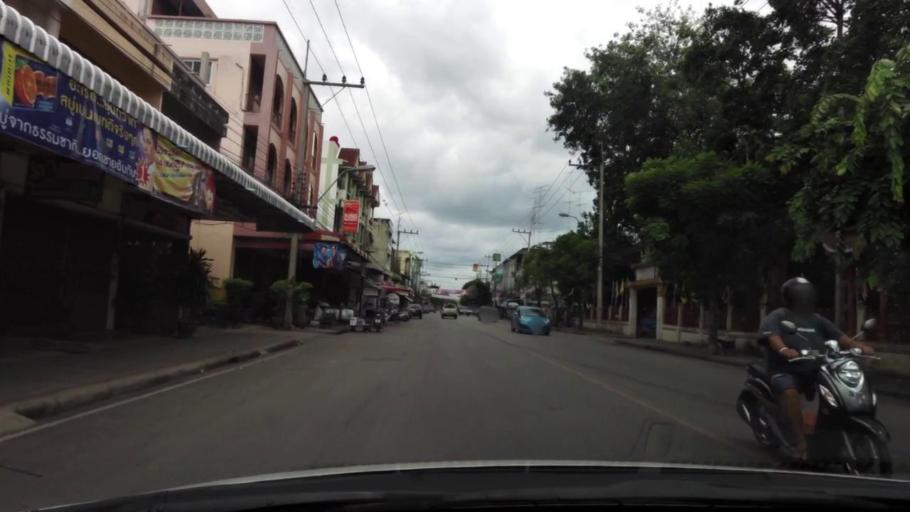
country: TH
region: Ratchaburi
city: Ratchaburi
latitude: 13.5377
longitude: 99.8295
